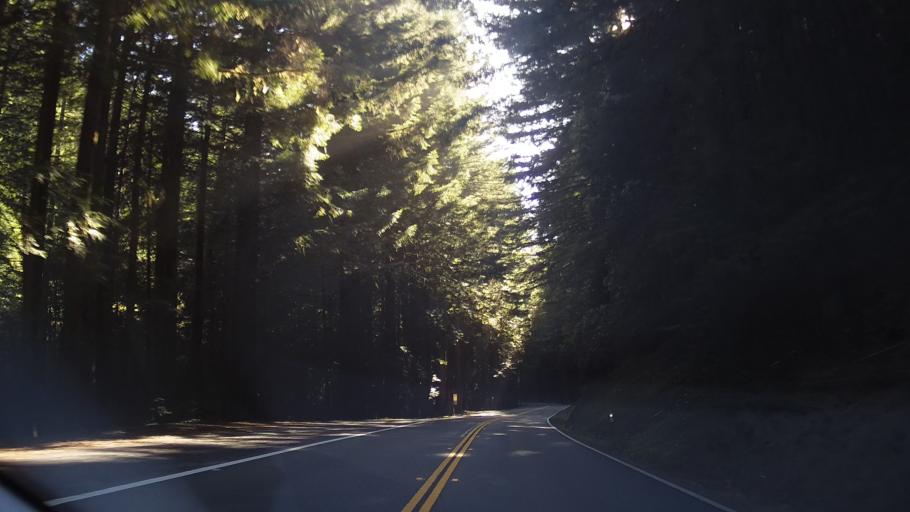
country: US
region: California
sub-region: Mendocino County
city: Brooktrails
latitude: 39.3489
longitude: -123.5796
